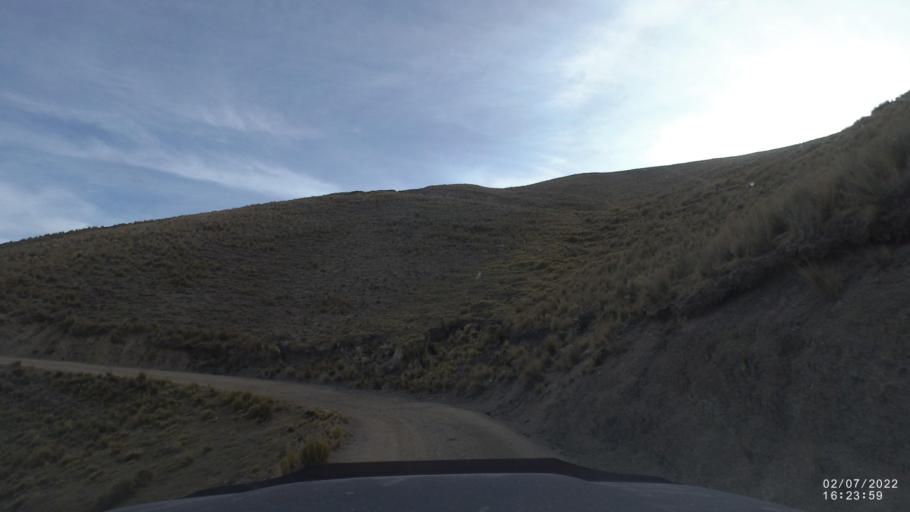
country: BO
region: Cochabamba
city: Irpa Irpa
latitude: -17.9391
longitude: -66.4613
